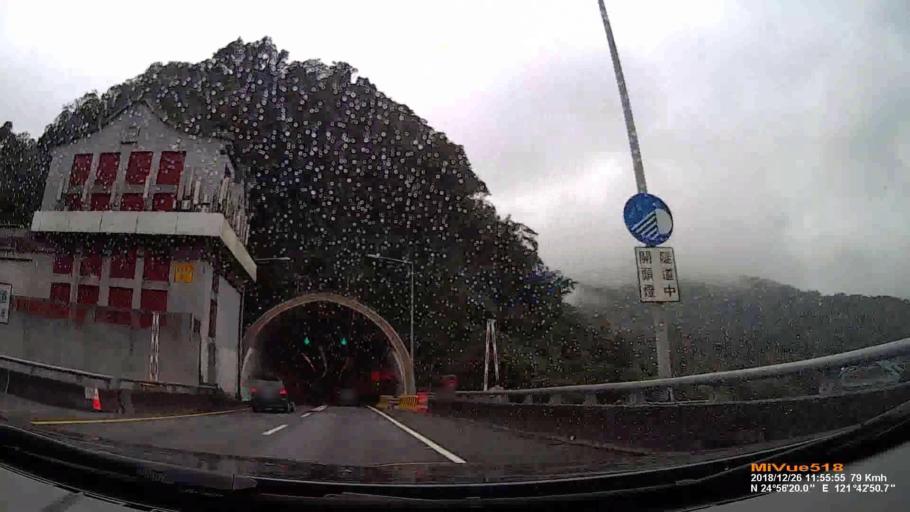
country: TW
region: Taiwan
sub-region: Yilan
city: Yilan
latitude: 24.9381
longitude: 121.7146
